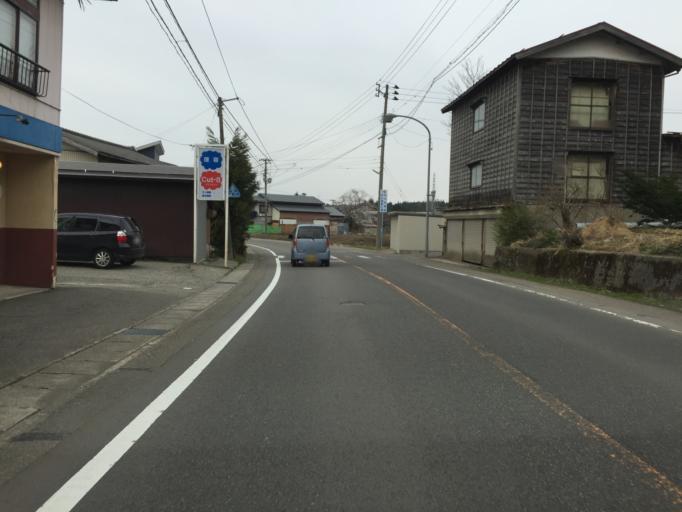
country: JP
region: Niigata
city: Tochio-honcho
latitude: 37.4879
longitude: 139.0134
